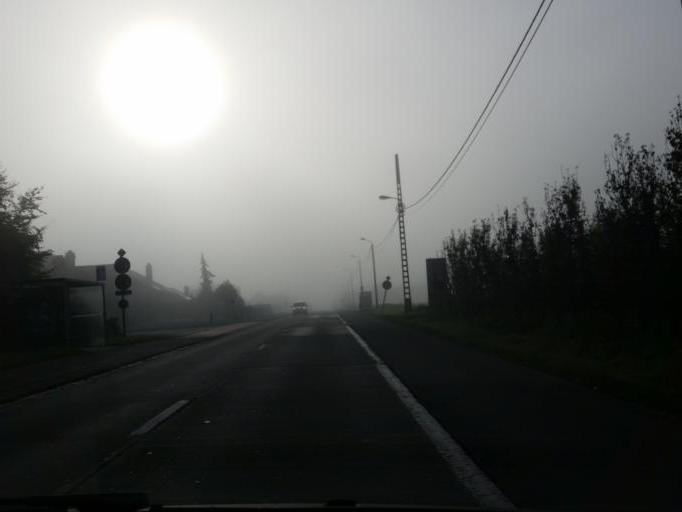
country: BE
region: Flanders
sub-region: Provincie Vlaams-Brabant
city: Opwijk
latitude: 50.9669
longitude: 4.1518
